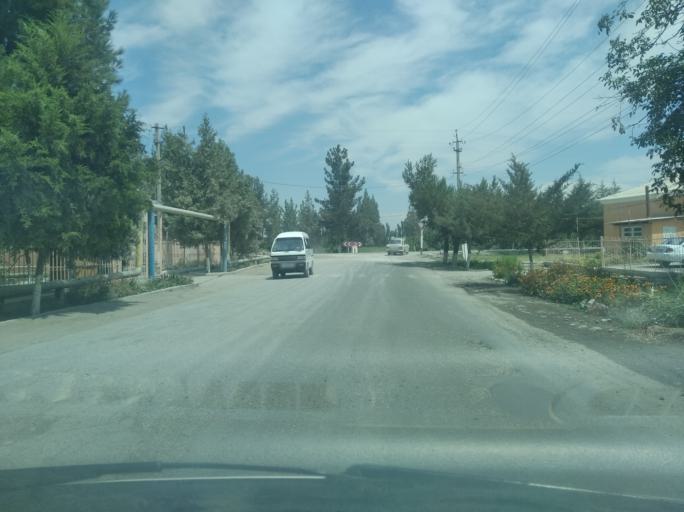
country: UZ
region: Andijon
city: Khujaobod
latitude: 40.6378
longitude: 72.4495
